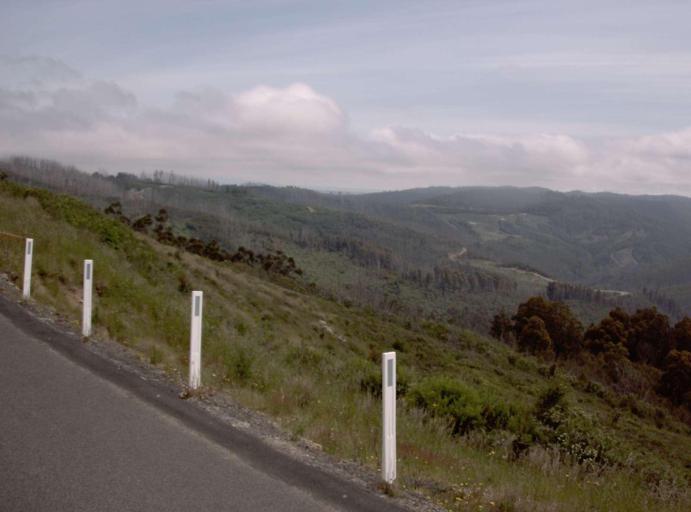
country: AU
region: Victoria
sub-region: Latrobe
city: Traralgon
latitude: -38.4033
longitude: 146.5634
